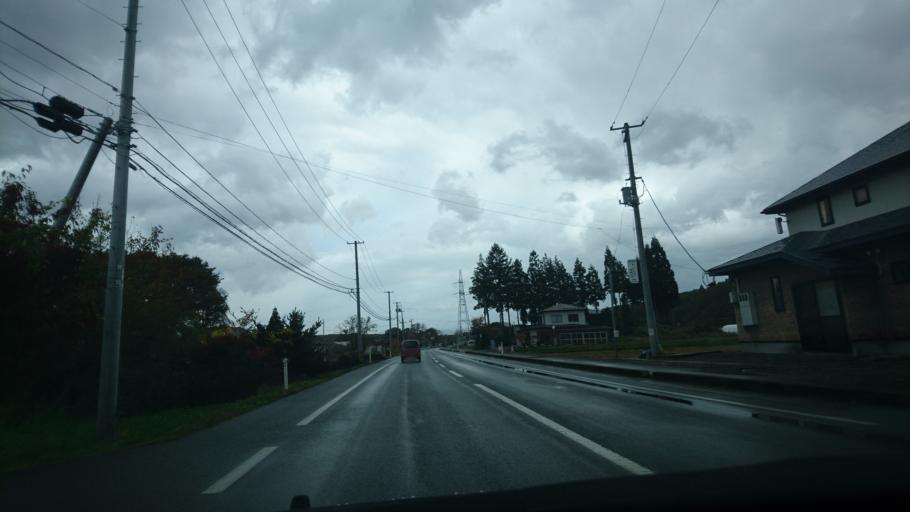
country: JP
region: Iwate
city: Shizukuishi
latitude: 39.6604
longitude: 140.9642
